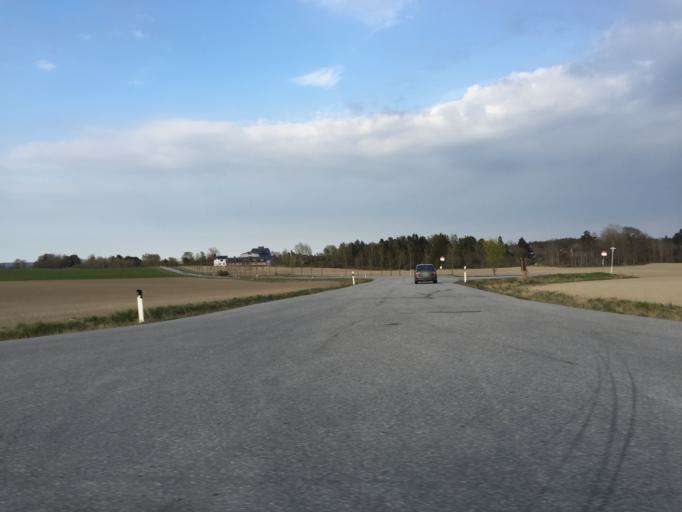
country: SE
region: Stockholm
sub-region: Sodertalje Kommun
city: Pershagen
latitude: 59.0662
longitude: 17.6062
